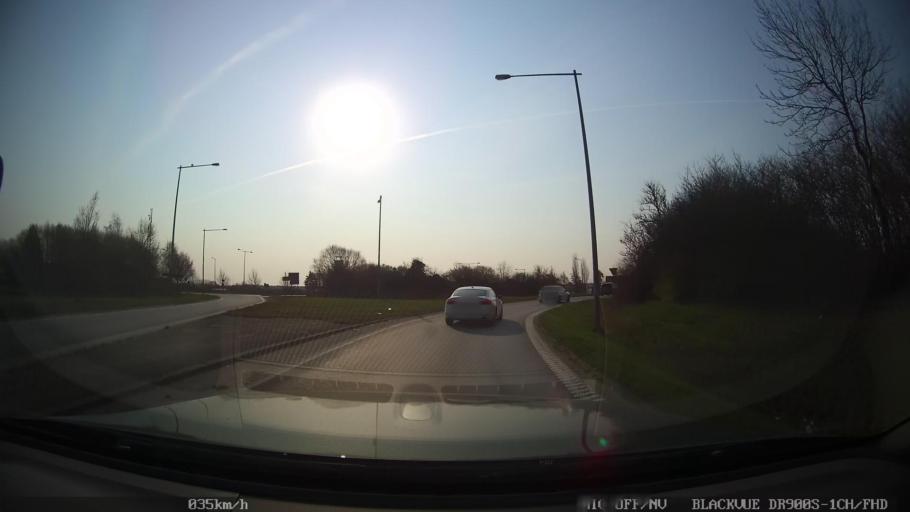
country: SE
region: Skane
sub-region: Ystads Kommun
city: Ystad
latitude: 55.4436
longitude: 13.8335
